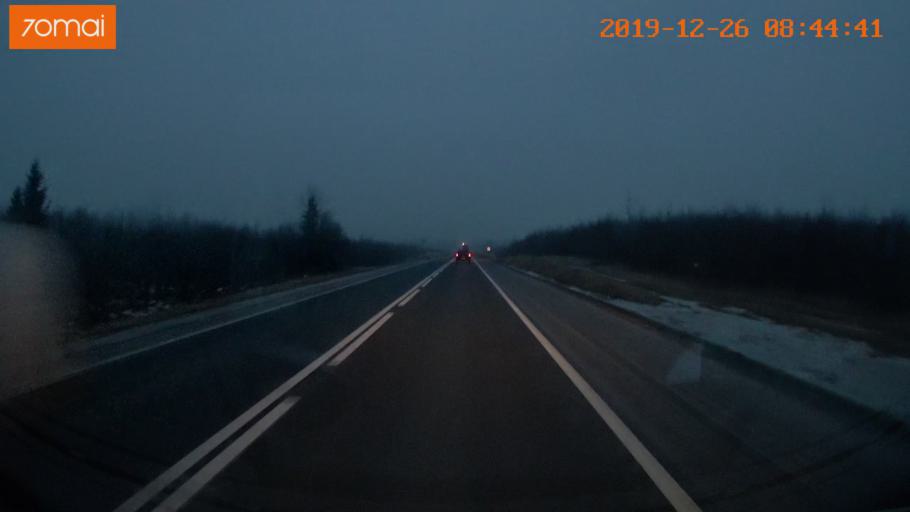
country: RU
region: Jaroslavl
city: Prechistoye
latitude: 58.5865
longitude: 40.3478
